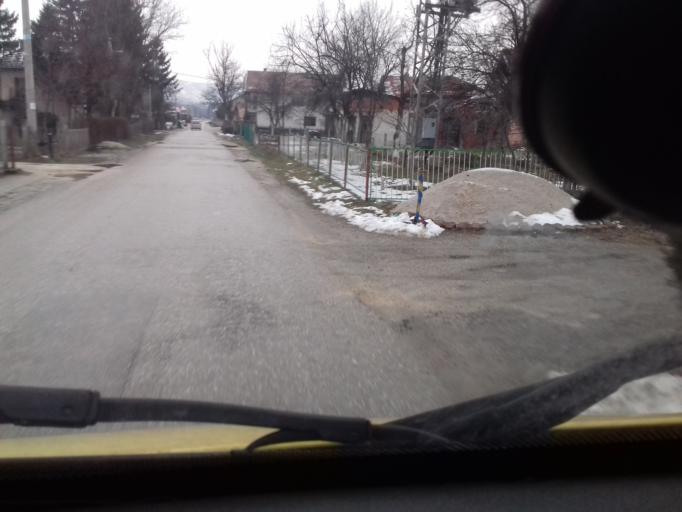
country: BA
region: Federation of Bosnia and Herzegovina
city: Vitez
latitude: 44.1557
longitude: 17.7851
